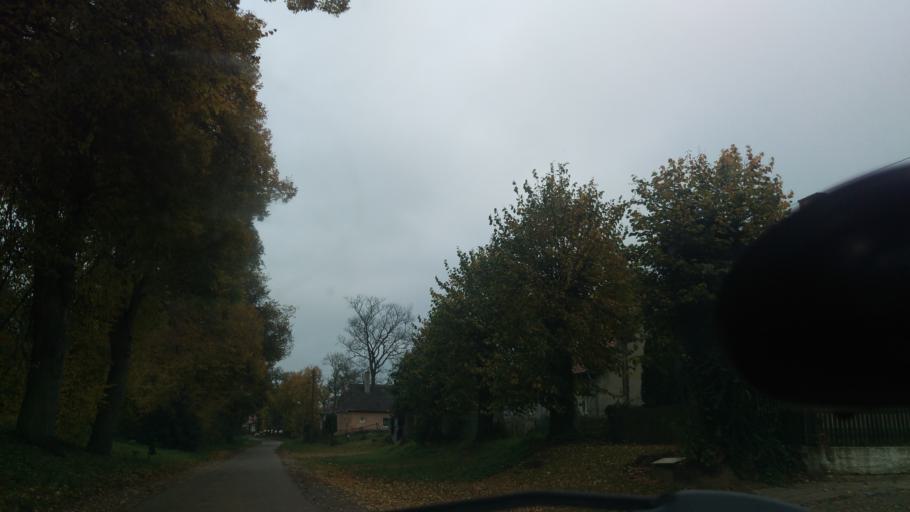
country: PL
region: West Pomeranian Voivodeship
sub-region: Powiat pyrzycki
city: Przelewice
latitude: 53.0491
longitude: 15.1106
